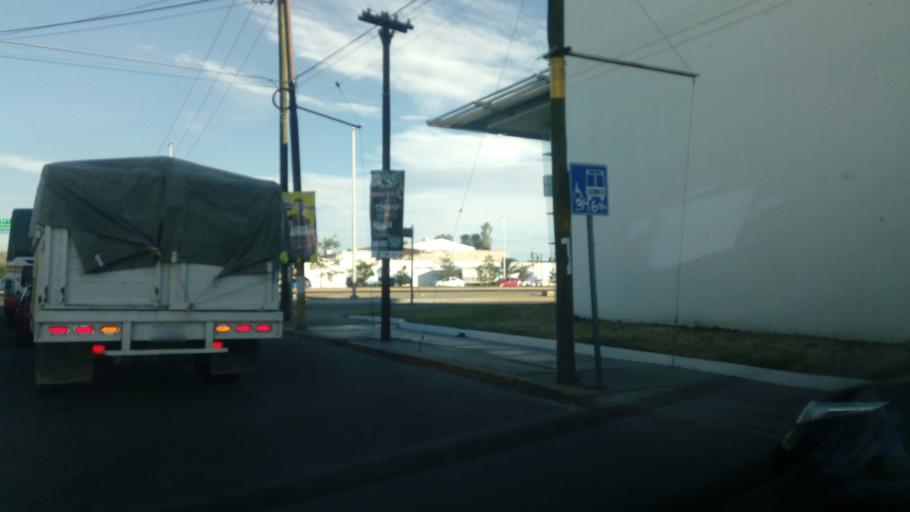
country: MX
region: Durango
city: Victoria de Durango
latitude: 24.0669
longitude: -104.6006
